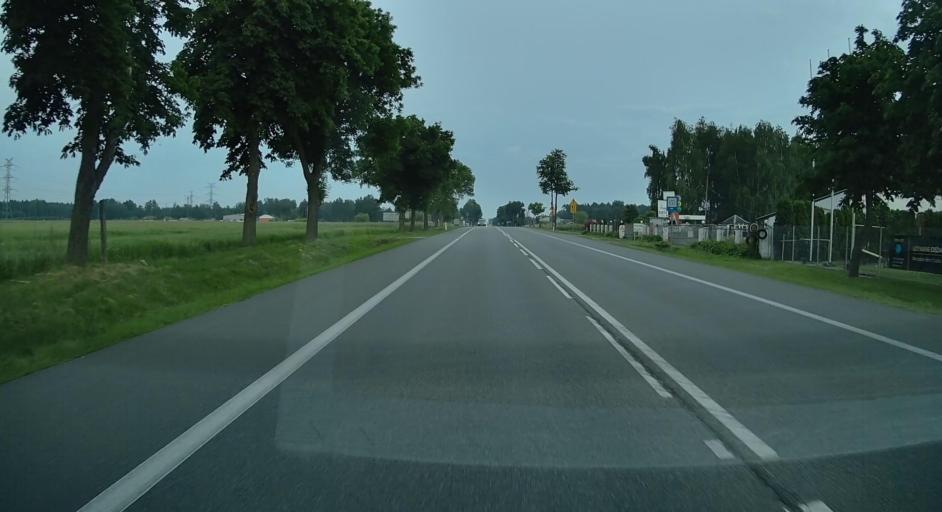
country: PL
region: Masovian Voivodeship
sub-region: Siedlce
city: Siedlce
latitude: 52.1262
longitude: 22.3436
